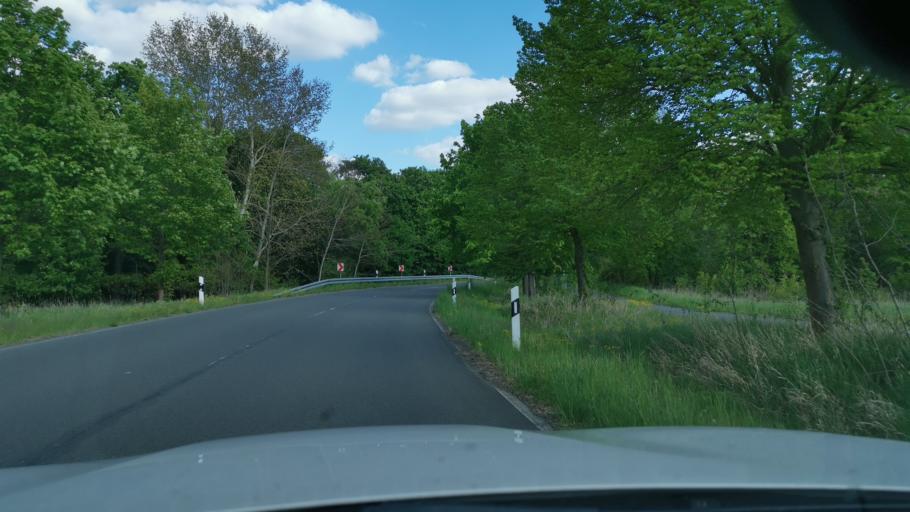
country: DE
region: Brandenburg
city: Niedergorsdorf
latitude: 51.9931
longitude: 13.0055
